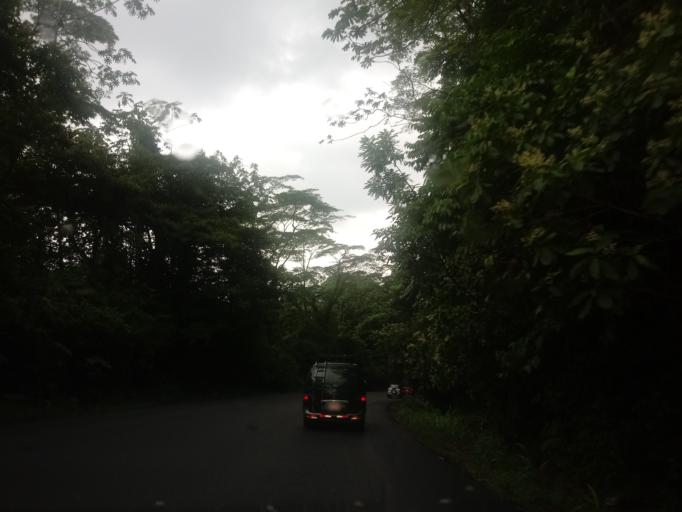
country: CR
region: San Jose
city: Dulce Nombre de Jesus
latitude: 10.1544
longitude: -83.9541
